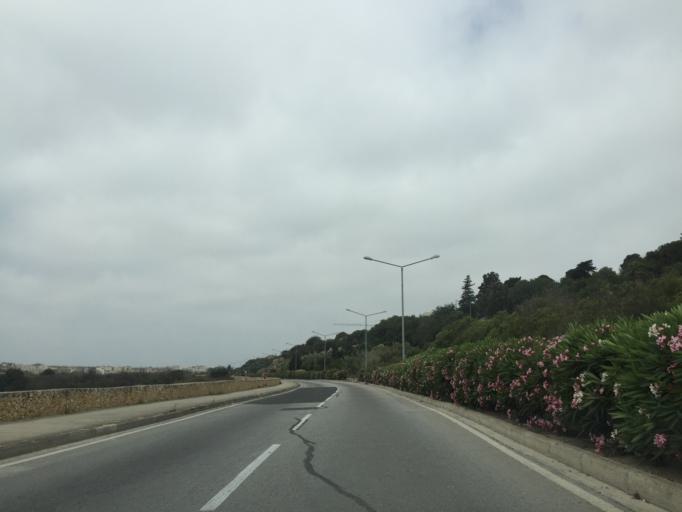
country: MT
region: L-Imtarfa
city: Imtarfa
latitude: 35.8906
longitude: 14.4013
